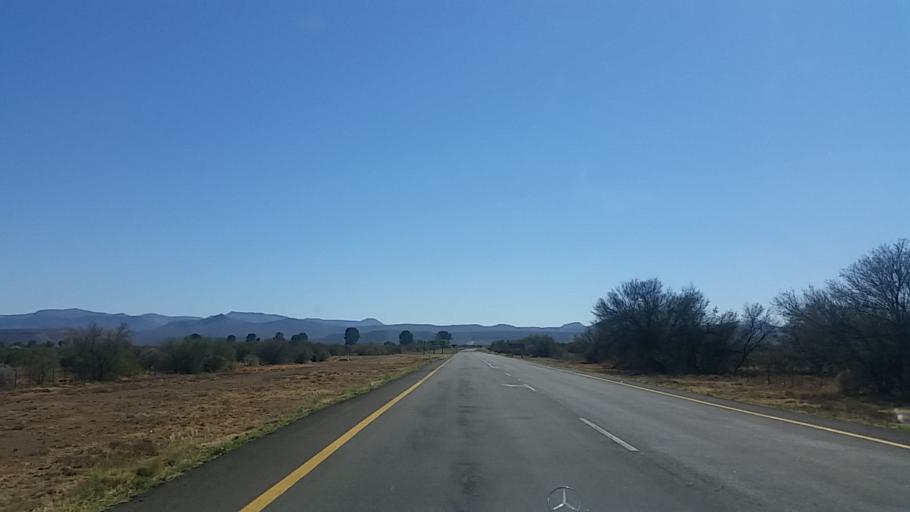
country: ZA
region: Eastern Cape
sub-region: Cacadu District Municipality
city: Graaff-Reinet
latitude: -32.1998
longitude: 24.5531
